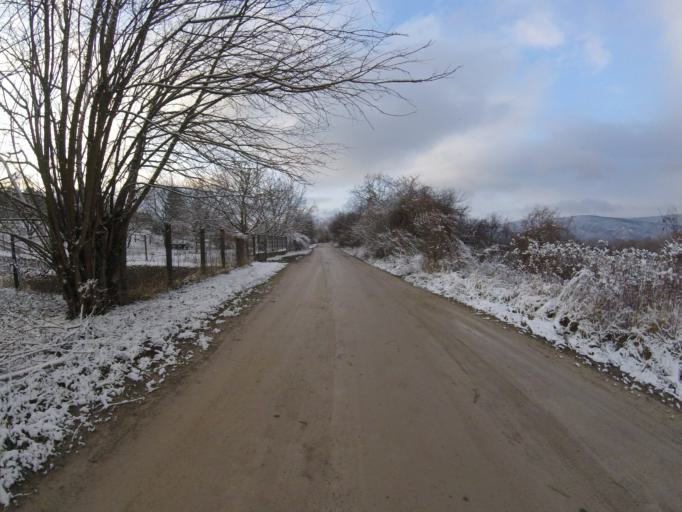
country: HU
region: Komarom-Esztergom
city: Esztergom
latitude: 47.8018
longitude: 18.7766
